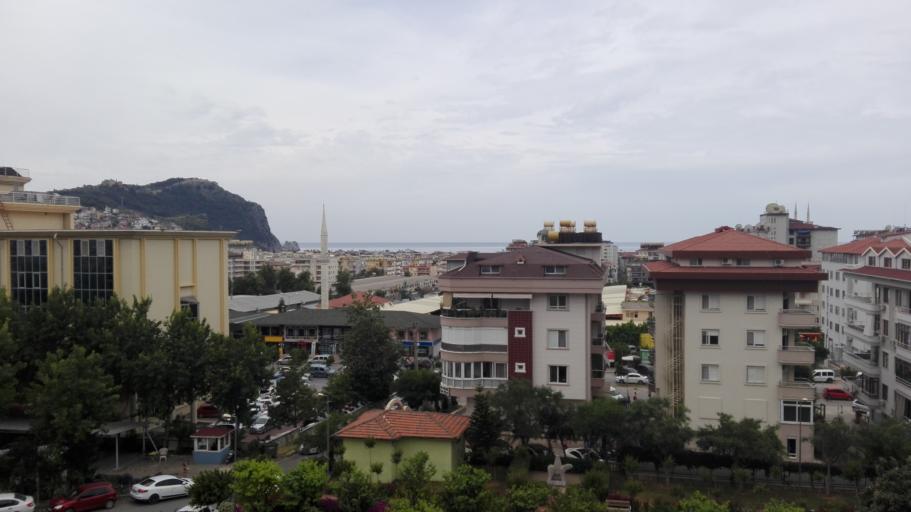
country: TR
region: Antalya
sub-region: Alanya
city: Alanya
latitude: 36.5566
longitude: 31.9901
